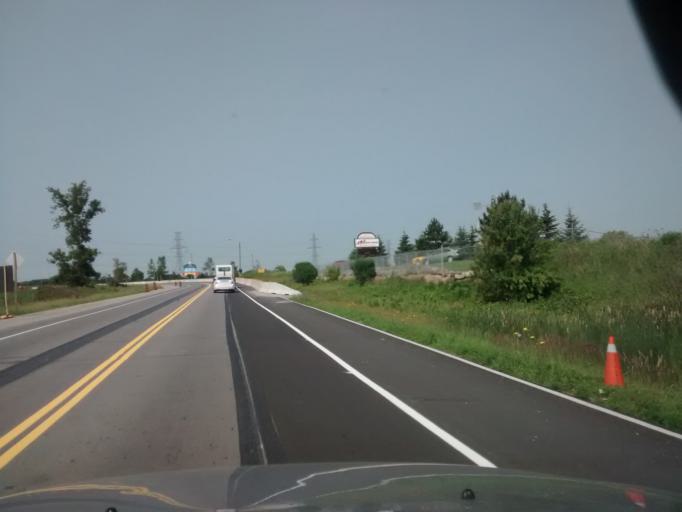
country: CA
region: Ontario
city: Hamilton
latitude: 43.1701
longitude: -79.7803
